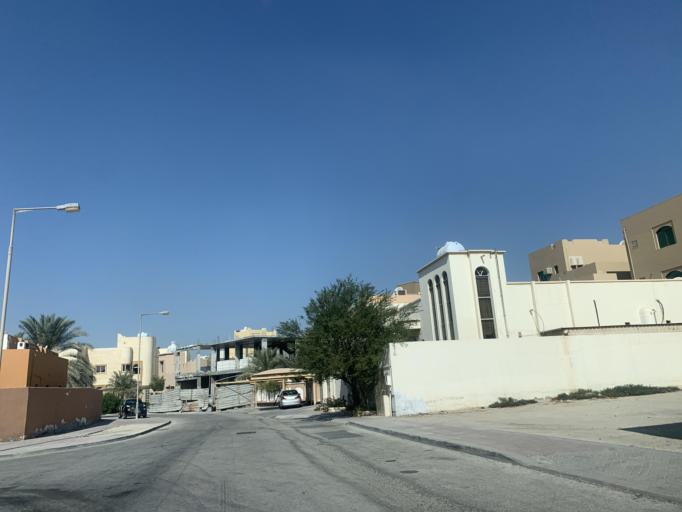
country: BH
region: Central Governorate
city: Madinat Hamad
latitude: 26.1206
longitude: 50.4954
